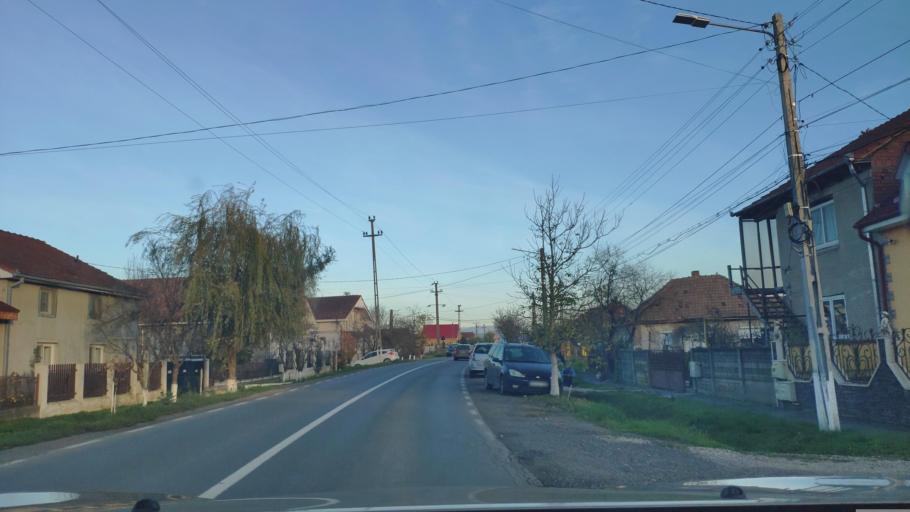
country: RO
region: Satu Mare
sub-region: Comuna Odoreu
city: Odoreu
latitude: 47.7928
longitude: 23.0025
